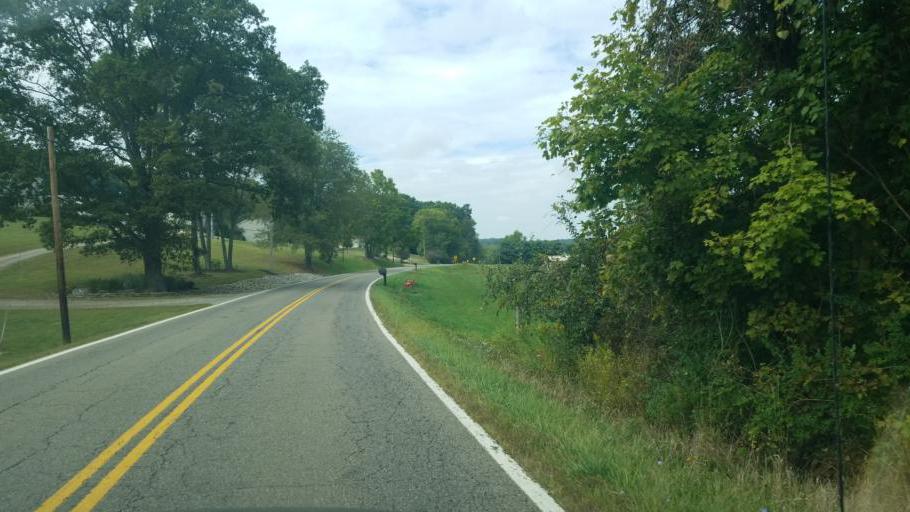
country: US
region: Ohio
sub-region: Licking County
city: Newark
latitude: 39.9982
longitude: -82.2785
